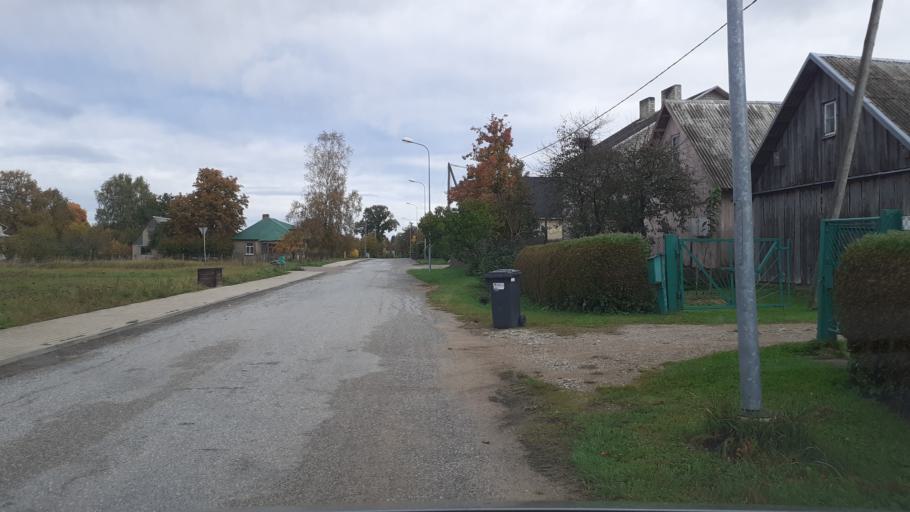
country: LV
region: Kuldigas Rajons
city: Kuldiga
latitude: 56.9642
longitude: 21.9937
